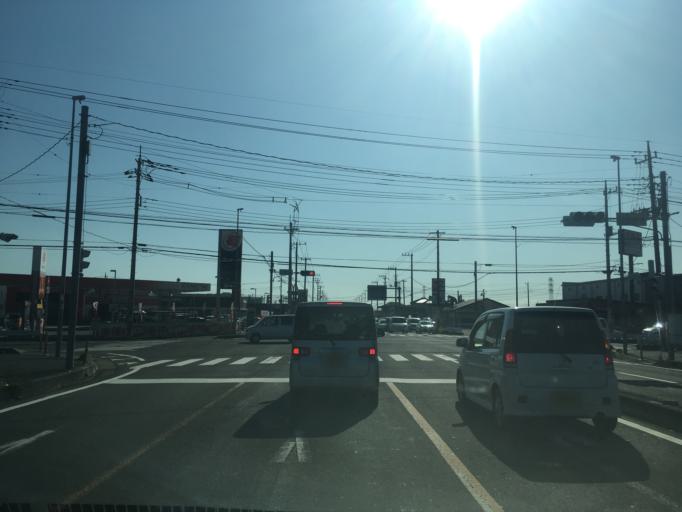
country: JP
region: Saitama
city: Kawagoe
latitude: 35.9319
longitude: 139.4681
